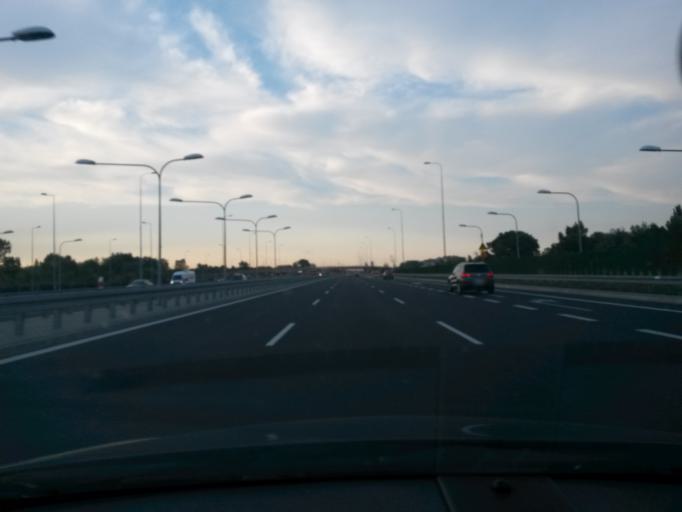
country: PL
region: Masovian Voivodeship
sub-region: Warszawa
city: Wlochy
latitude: 52.1633
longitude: 20.9867
